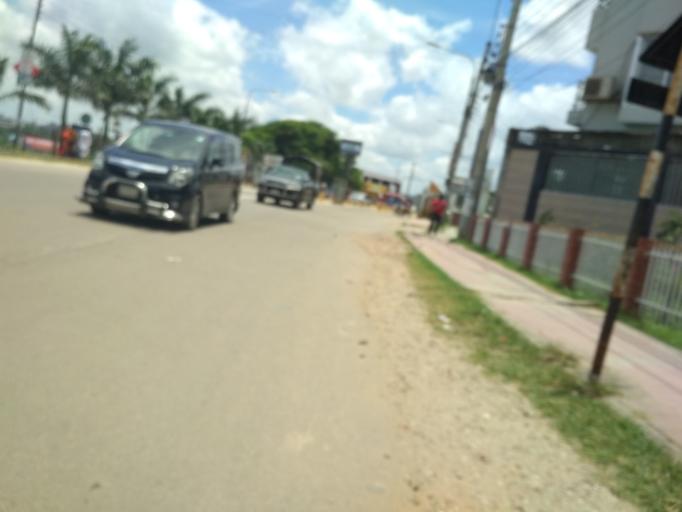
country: BD
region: Dhaka
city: Tungi
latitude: 23.8375
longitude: 90.3756
